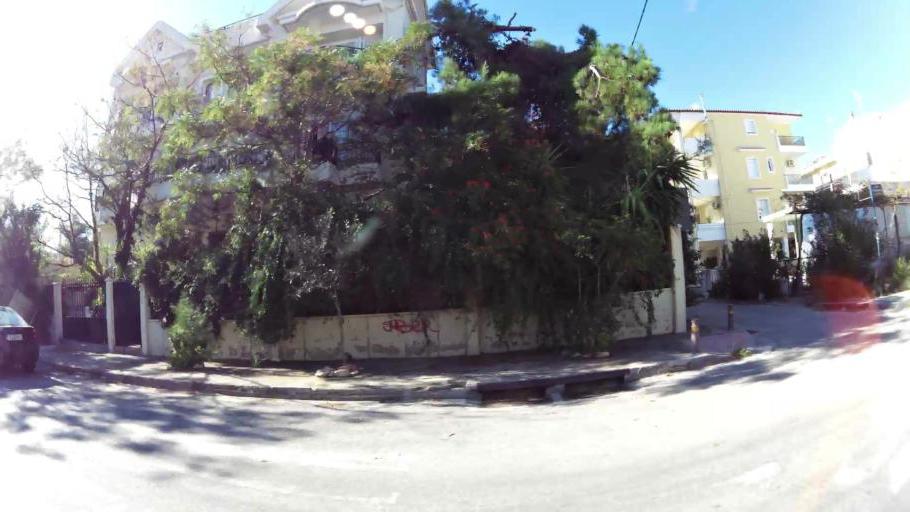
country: GR
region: Attica
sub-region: Nomarchia Athinas
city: Vrilissia
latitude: 38.0287
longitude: 23.8331
